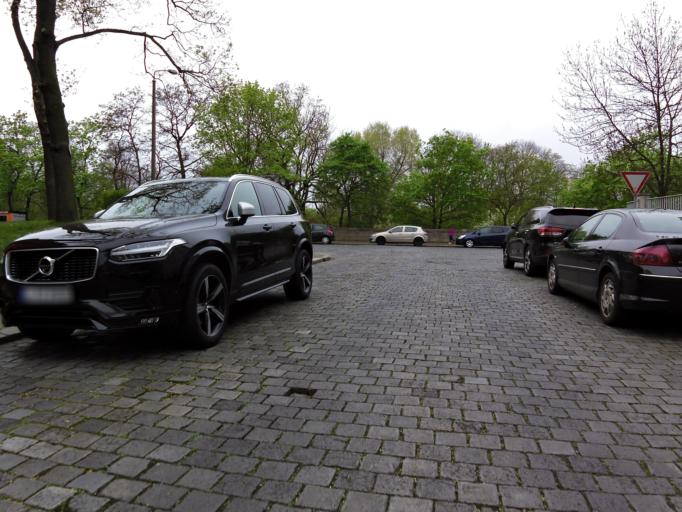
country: DE
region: Saxony
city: Leipzig
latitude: 51.3539
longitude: 12.3679
